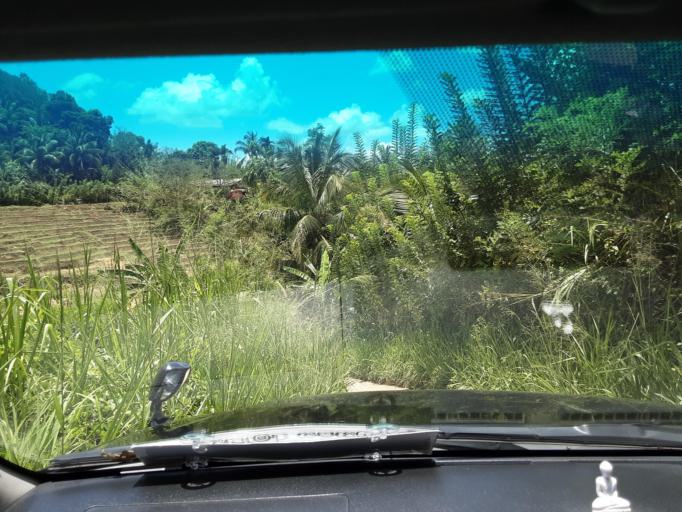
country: LK
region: Uva
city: Haputale
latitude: 6.8250
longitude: 81.1093
